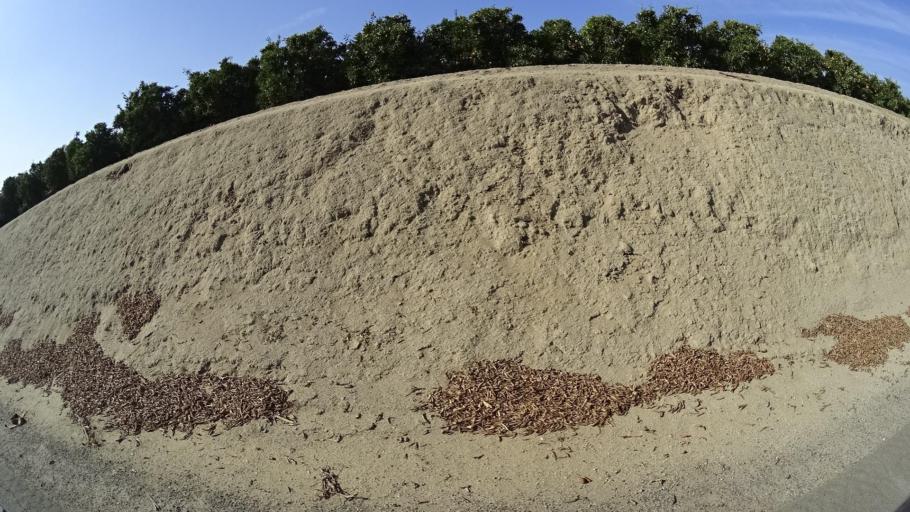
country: US
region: California
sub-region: Kern County
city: McFarland
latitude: 35.6472
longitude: -119.1336
